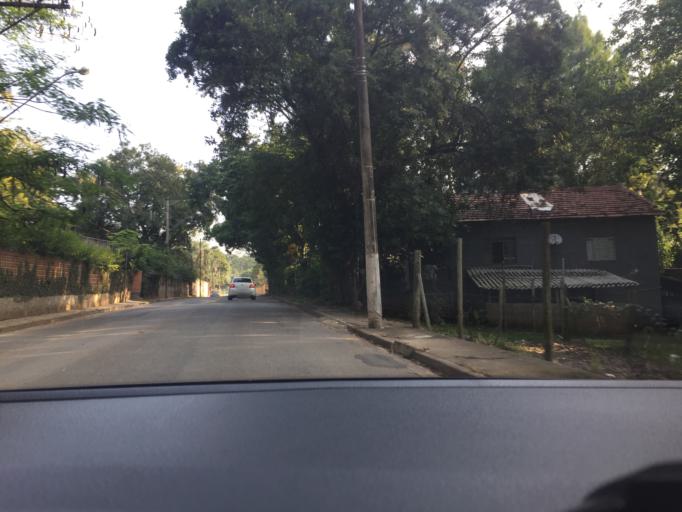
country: BR
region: Sao Paulo
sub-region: Valinhos
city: Valinhos
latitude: -23.0027
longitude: -47.0092
